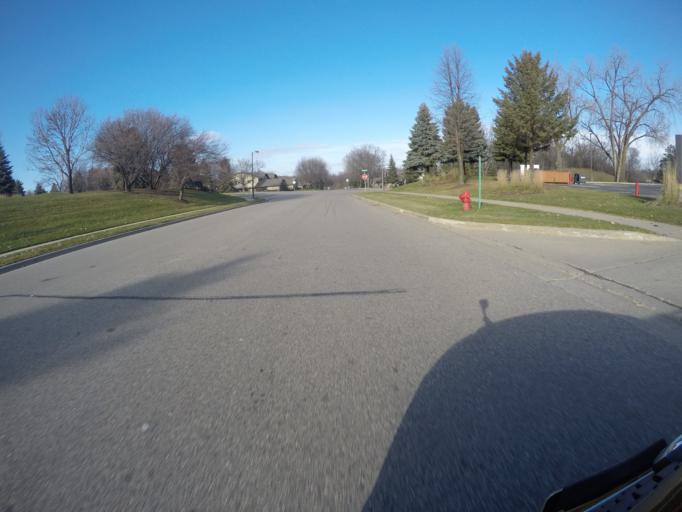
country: US
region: Minnesota
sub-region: Hennepin County
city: Eden Prairie
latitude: 44.8657
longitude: -93.4468
